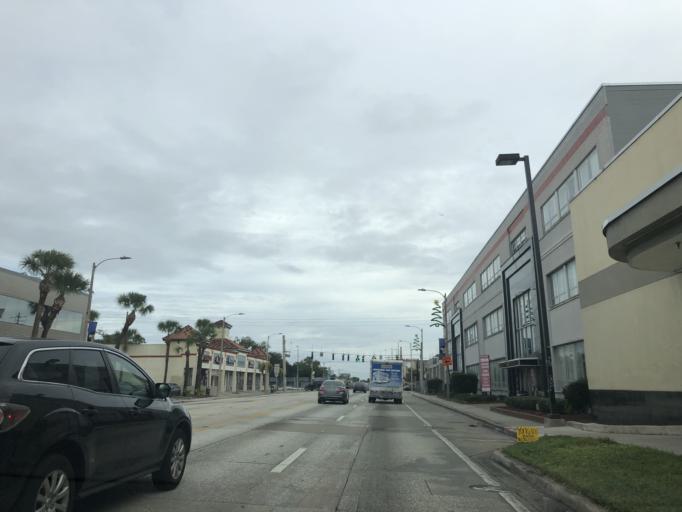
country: US
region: Florida
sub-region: Orange County
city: Orlando
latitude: 28.5531
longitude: -81.3615
